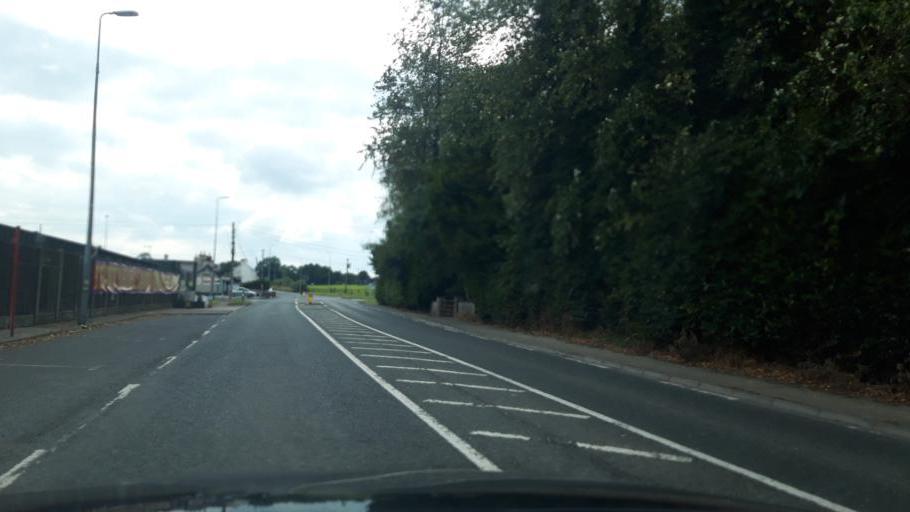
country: IE
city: Ballylinan
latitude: 52.8638
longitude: -7.1068
